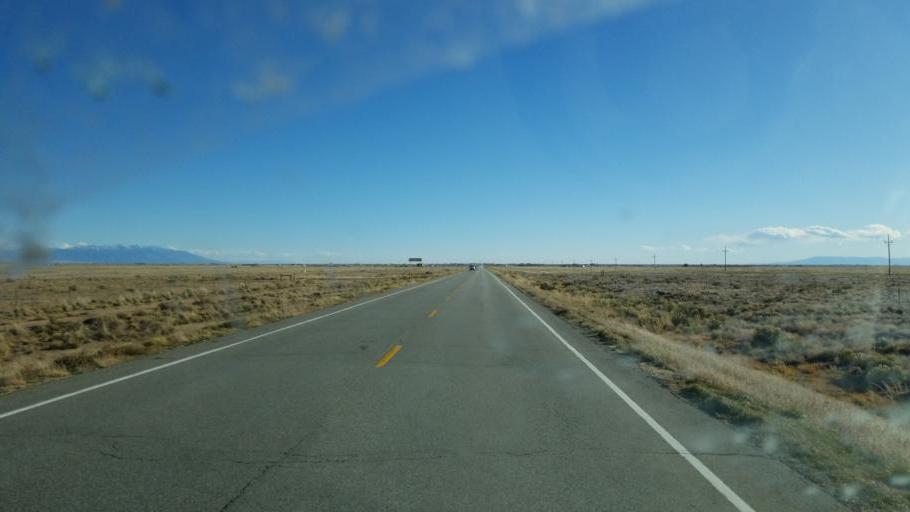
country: US
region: Colorado
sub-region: Saguache County
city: Saguache
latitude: 38.1641
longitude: -105.9268
